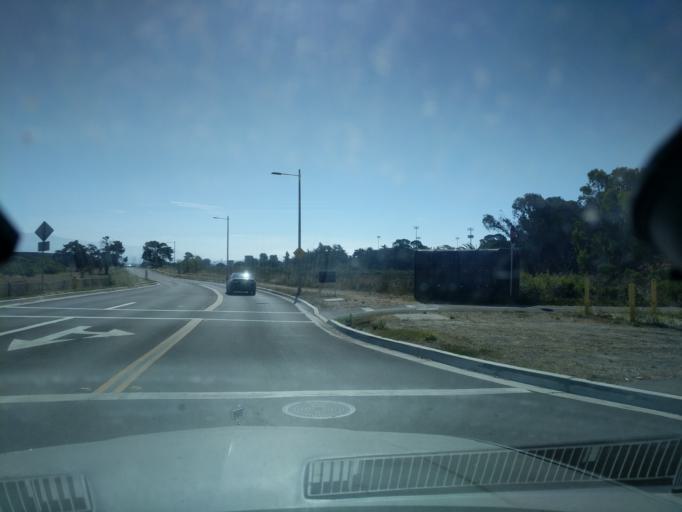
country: US
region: California
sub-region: Santa Barbara County
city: Isla Vista
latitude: 34.4220
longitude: -119.8597
